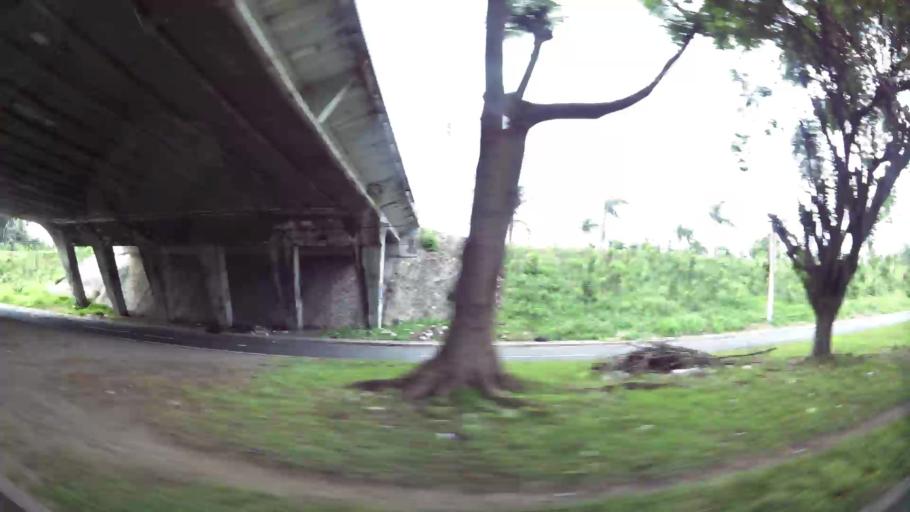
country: DO
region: Santiago
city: Licey al Medio
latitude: 19.4146
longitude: -70.6435
